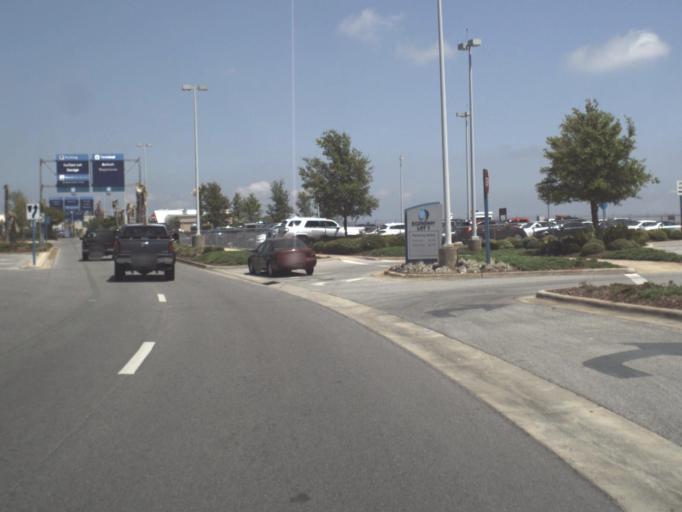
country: US
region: Florida
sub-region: Escambia County
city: Brent
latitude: 30.4744
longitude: -87.1982
